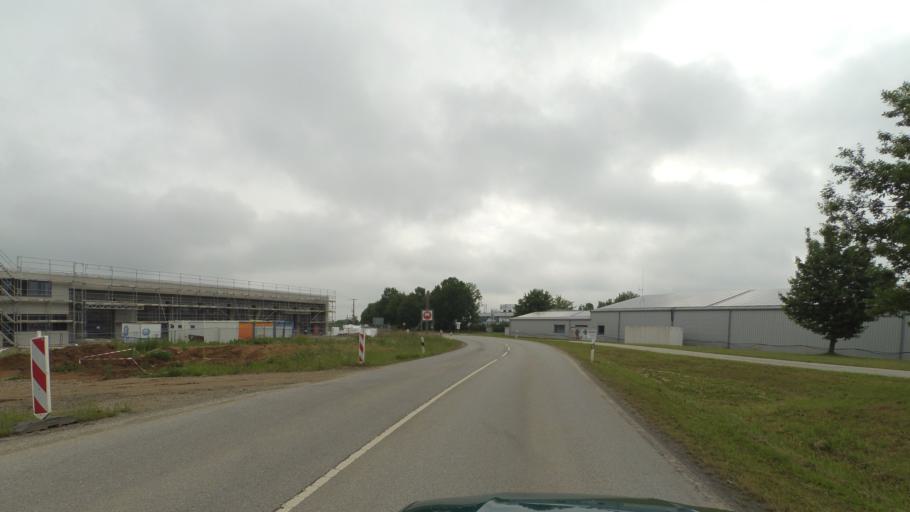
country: DE
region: Bavaria
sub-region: Lower Bavaria
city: Geiselhoring
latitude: 48.8145
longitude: 12.3889
